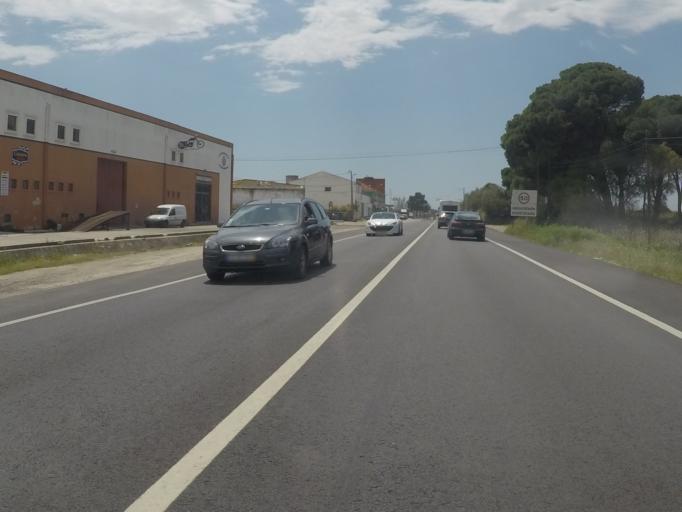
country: PT
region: Setubal
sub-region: Setubal
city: Setubal
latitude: 38.5532
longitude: -8.8066
